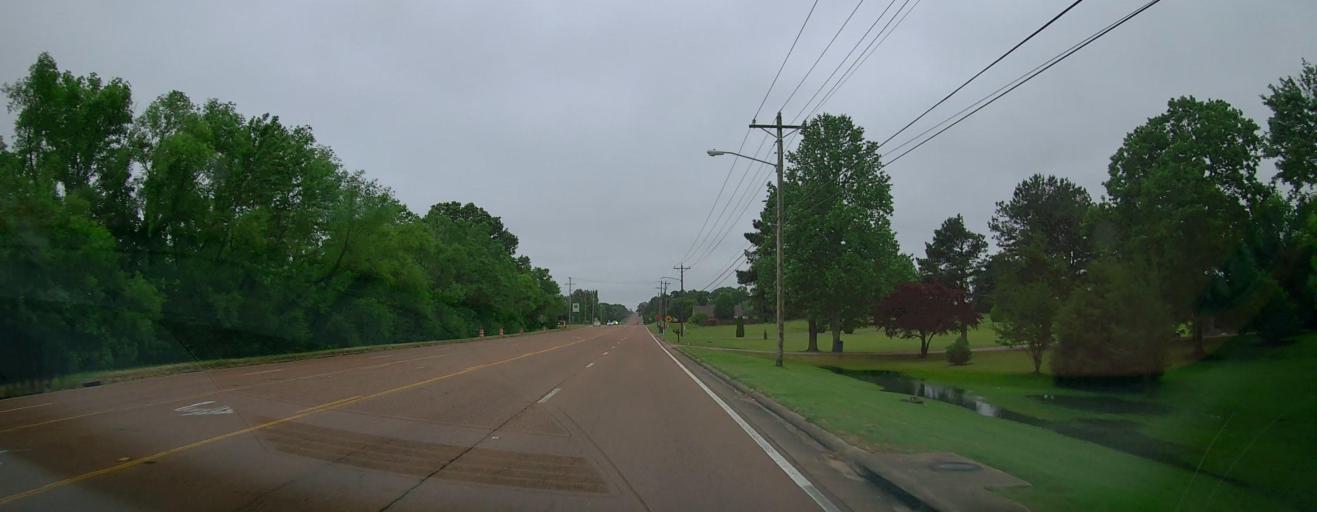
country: US
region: Mississippi
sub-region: De Soto County
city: Olive Branch
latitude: 34.9525
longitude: -89.7951
